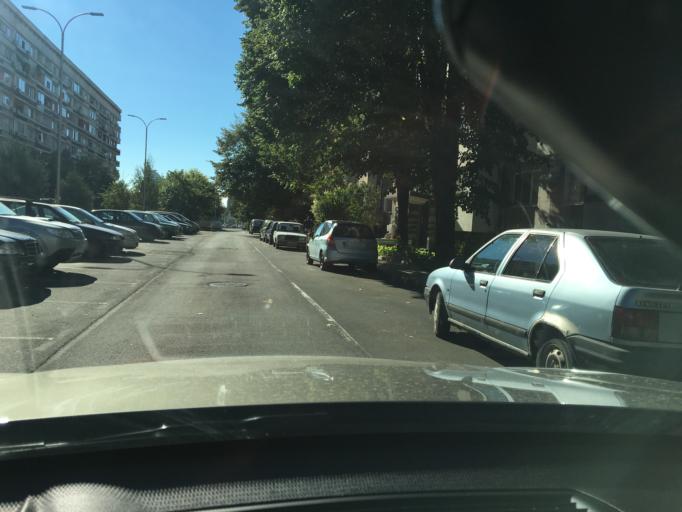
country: BG
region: Burgas
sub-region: Obshtina Burgas
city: Burgas
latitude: 42.5230
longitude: 27.4536
